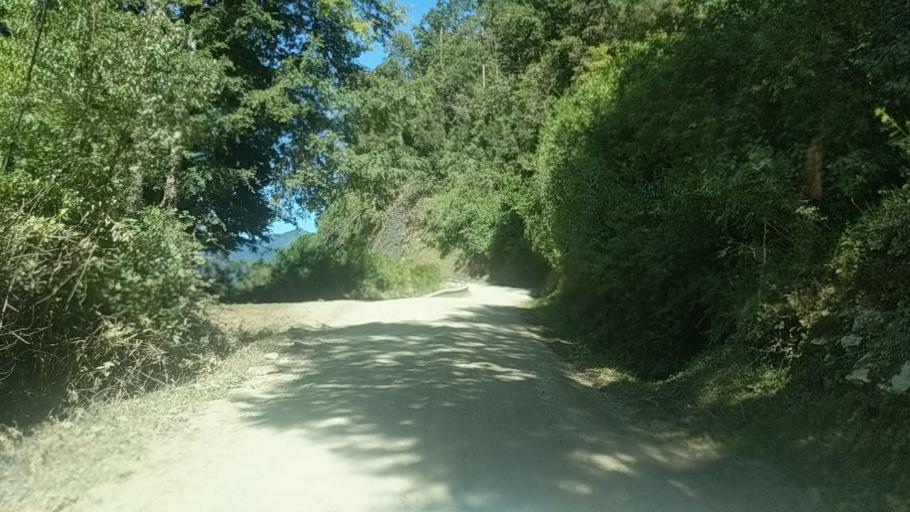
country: CL
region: Araucania
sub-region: Provincia de Cautin
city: Pucon
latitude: -39.0627
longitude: -71.7096
